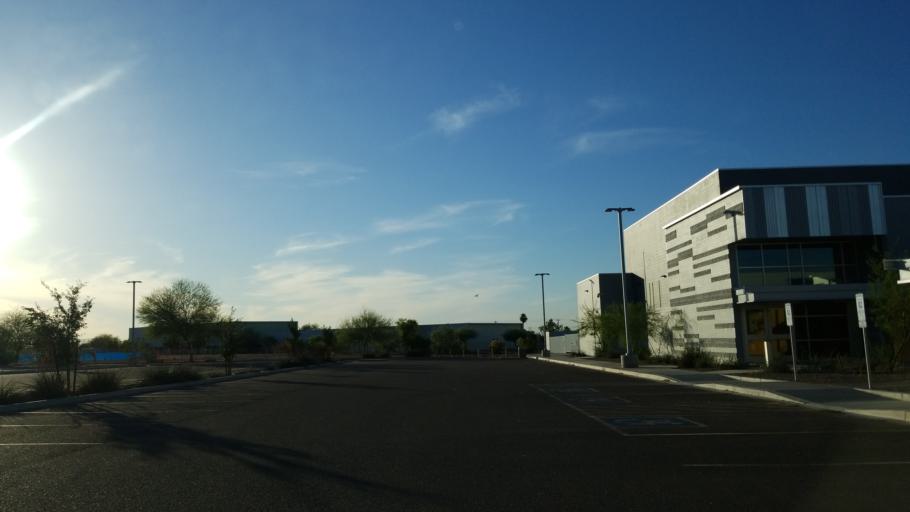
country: US
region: Arizona
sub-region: Maricopa County
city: Guadalupe
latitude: 33.3840
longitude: -112.0335
